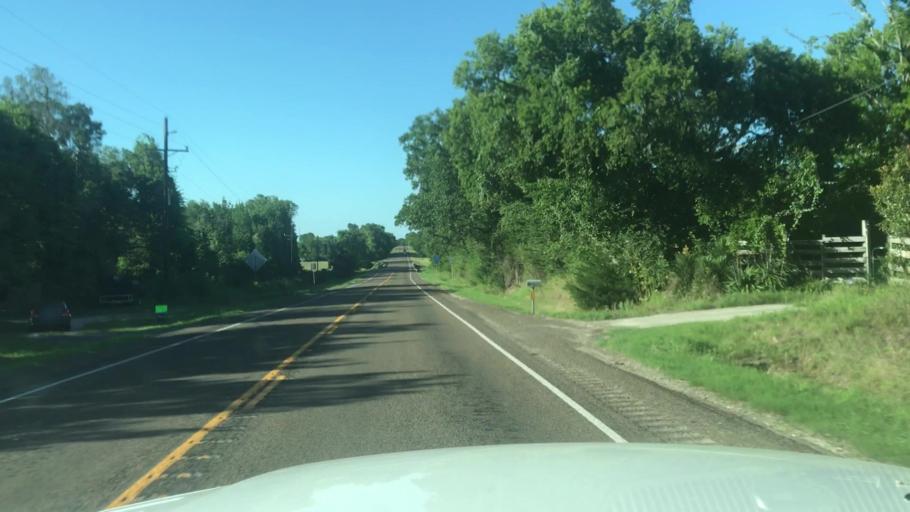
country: US
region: Texas
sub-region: Grimes County
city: Anderson
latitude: 30.6177
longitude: -95.8855
